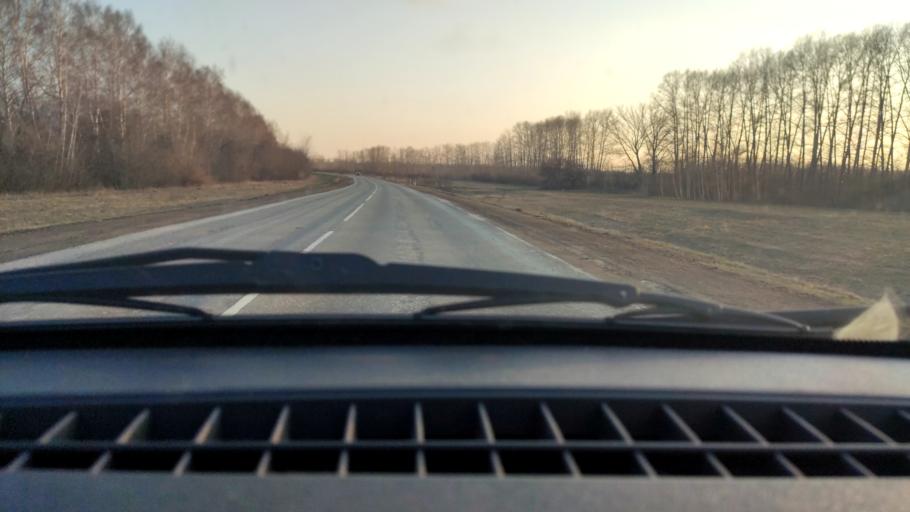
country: RU
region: Bashkortostan
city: Davlekanovo
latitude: 54.3523
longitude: 55.1819
